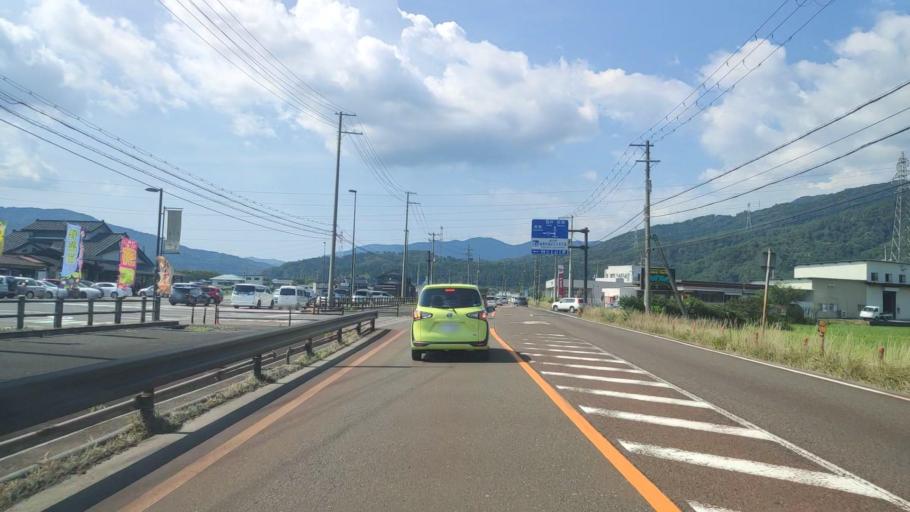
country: JP
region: Fukui
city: Tsuruga
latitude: 35.5203
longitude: 136.1635
